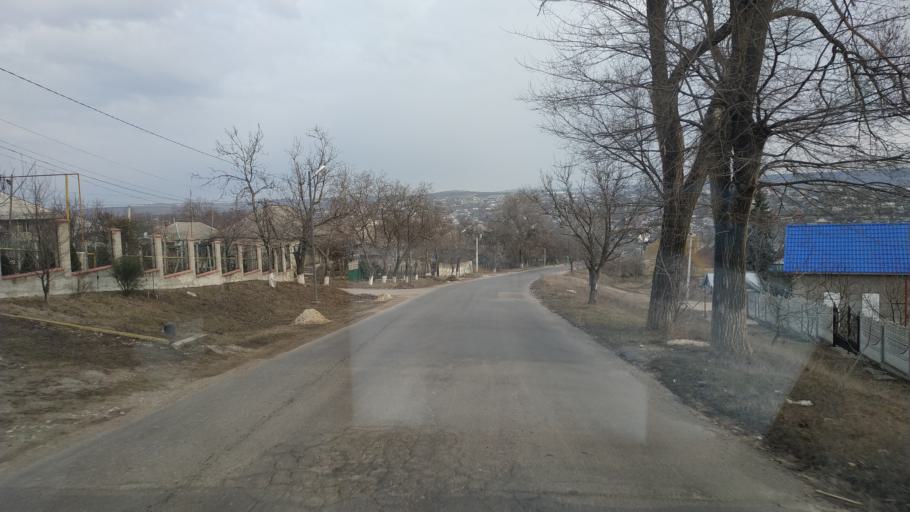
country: MD
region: Chisinau
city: Singera
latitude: 46.9542
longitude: 29.0577
